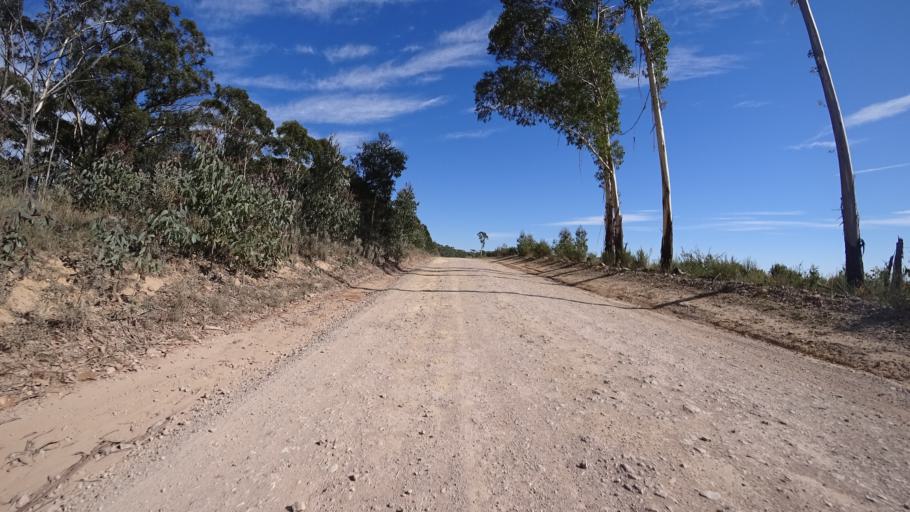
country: AU
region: New South Wales
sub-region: Lithgow
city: Lithgow
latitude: -33.4131
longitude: 150.2017
